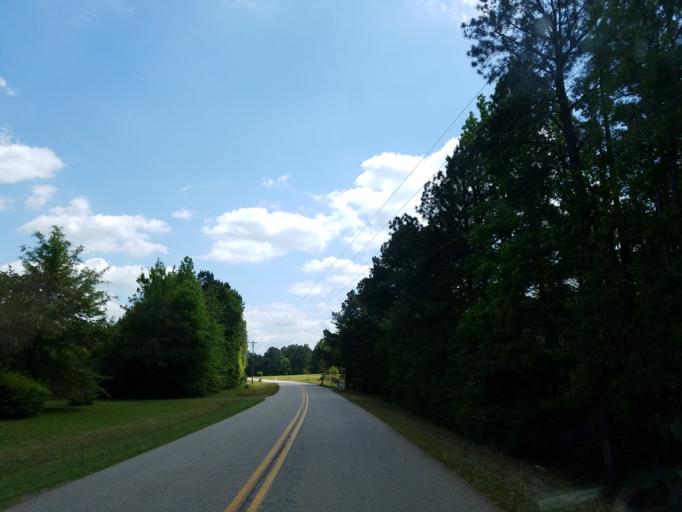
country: US
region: Georgia
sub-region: Monroe County
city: Forsyth
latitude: 33.1053
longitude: -83.9674
